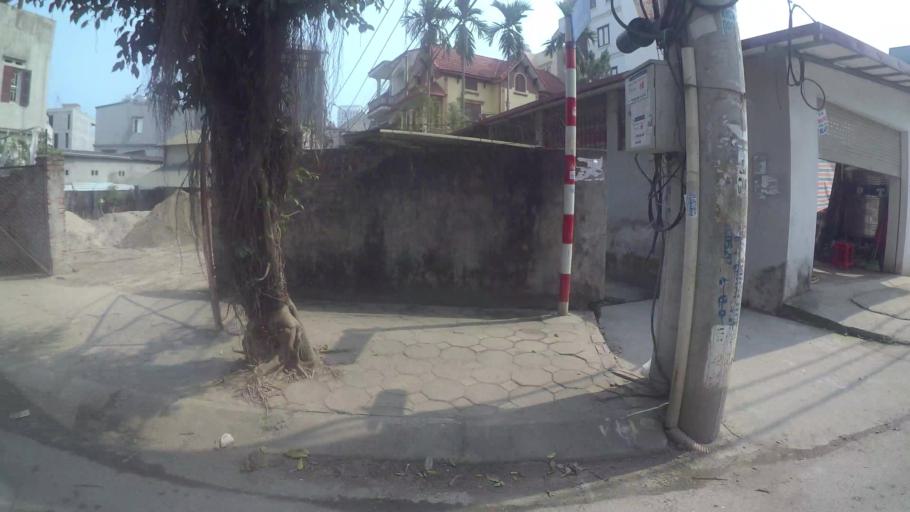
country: VN
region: Ha Noi
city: Tay Ho
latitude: 21.0885
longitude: 105.8105
